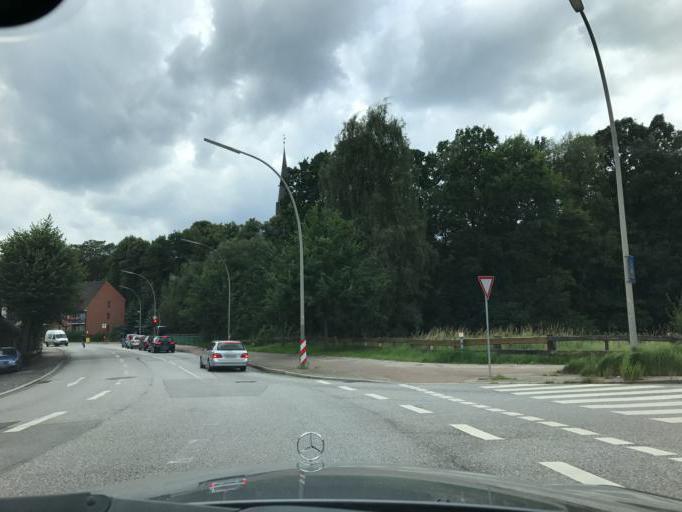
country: DE
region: Schleswig-Holstein
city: Oststeinbek
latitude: 53.5298
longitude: 10.1306
